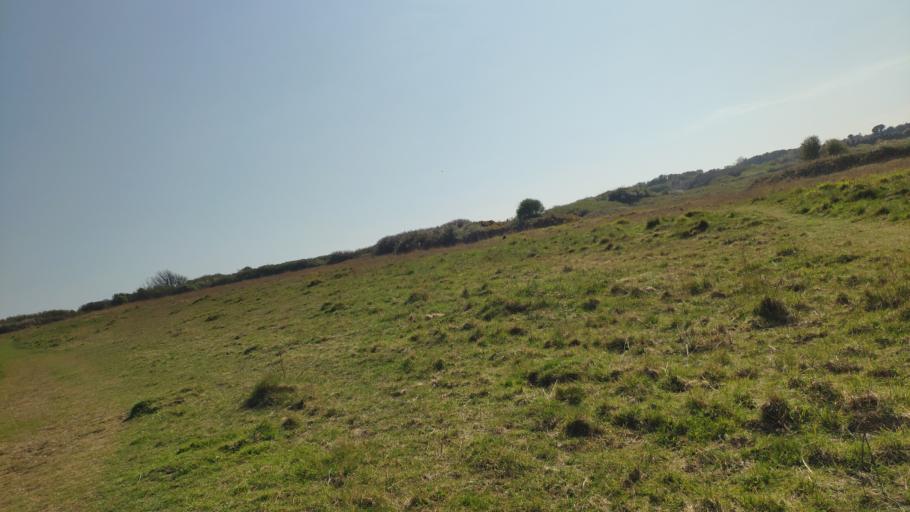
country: GB
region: England
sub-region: Dorset
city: Swanage
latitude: 50.5983
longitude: -1.9608
